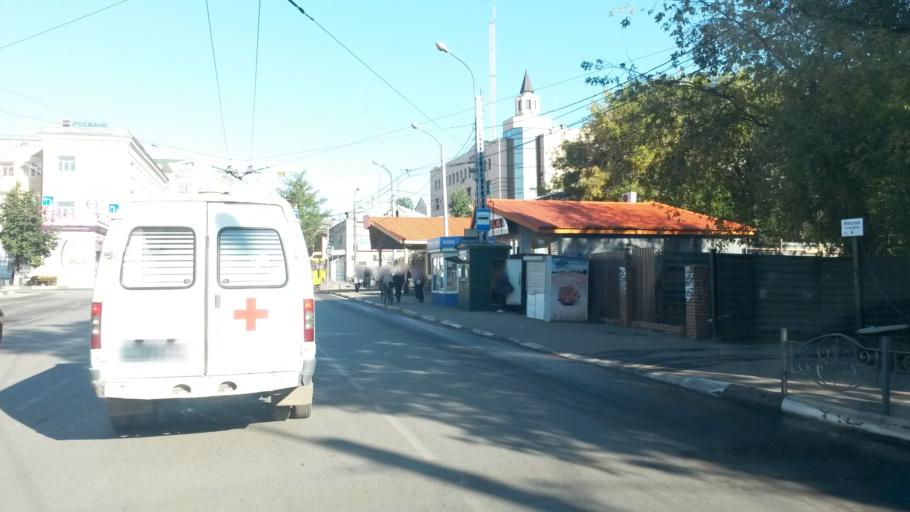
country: RU
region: Ivanovo
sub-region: Gorod Ivanovo
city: Ivanovo
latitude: 56.9933
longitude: 40.9758
